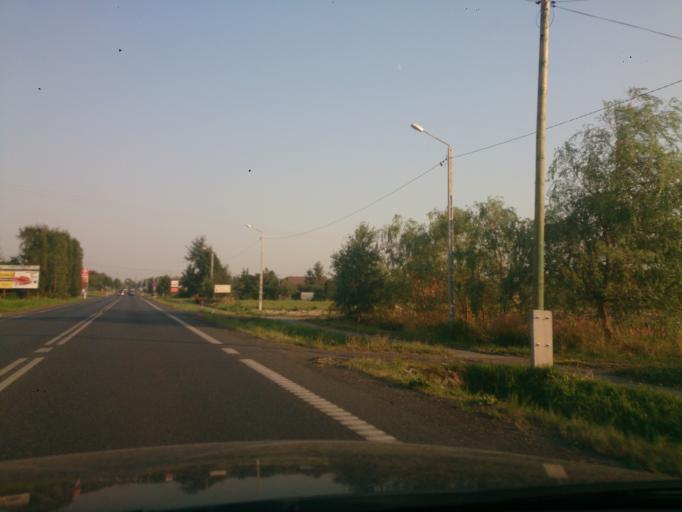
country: PL
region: Subcarpathian Voivodeship
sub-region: Powiat kolbuszowski
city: Kolbuszowa
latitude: 50.2594
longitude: 21.7642
